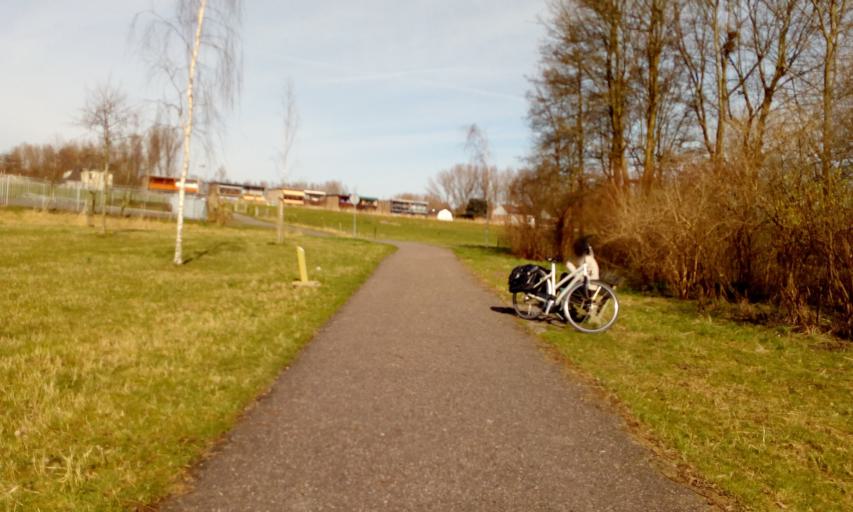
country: NL
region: South Holland
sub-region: Gemeente Lansingerland
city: Bergschenhoek
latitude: 51.9632
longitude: 4.5259
